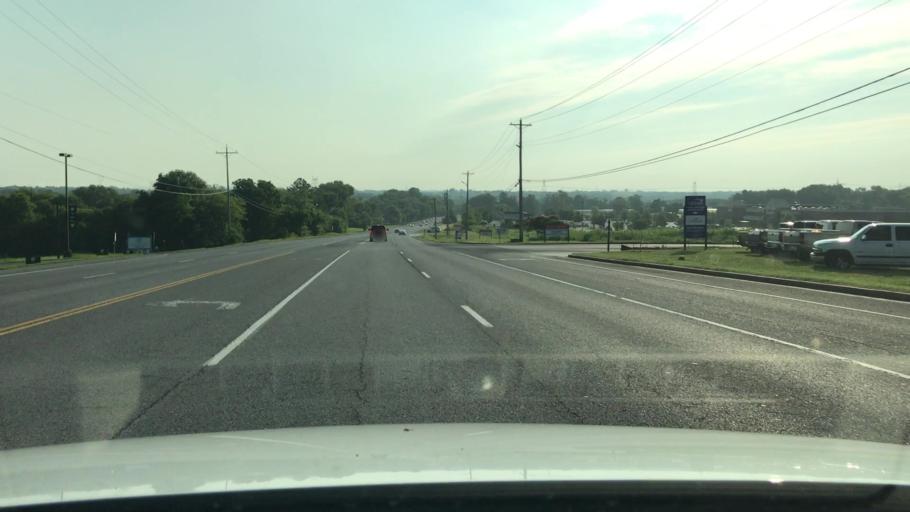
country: US
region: Tennessee
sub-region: Sumner County
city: Shackle Island
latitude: 36.3429
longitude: -86.5311
